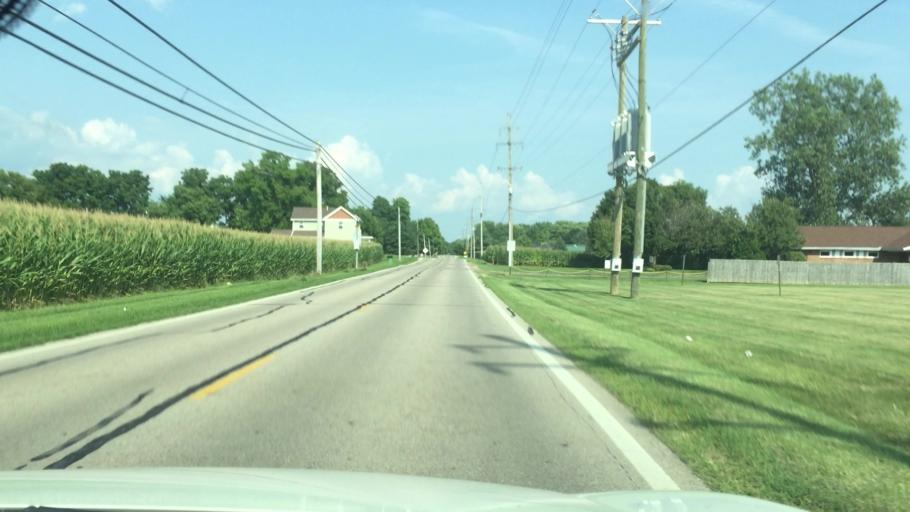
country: US
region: Ohio
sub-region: Clark County
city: Northridge
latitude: 39.9942
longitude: -83.7500
